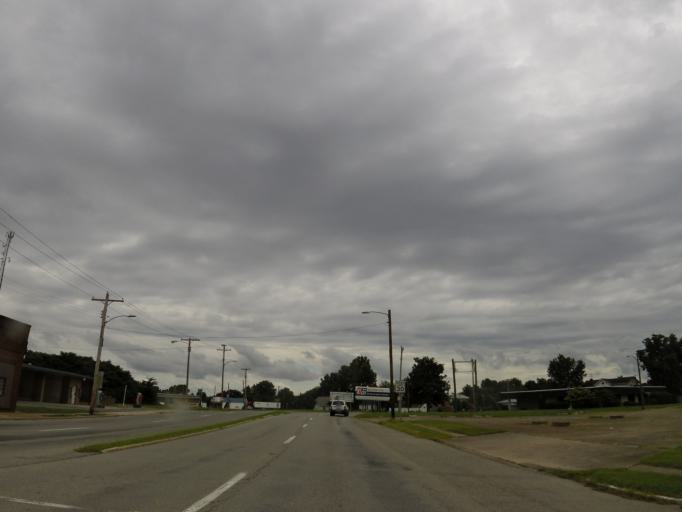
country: US
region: Illinois
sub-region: Alexander County
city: Cairo
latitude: 37.0068
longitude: -89.1778
